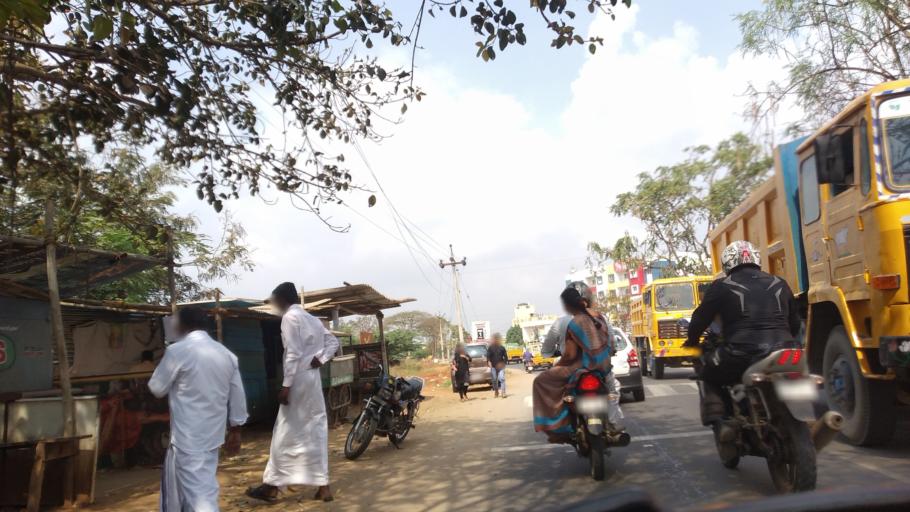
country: IN
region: Tamil Nadu
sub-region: Coimbatore
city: Perur
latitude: 10.9442
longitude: 76.9396
